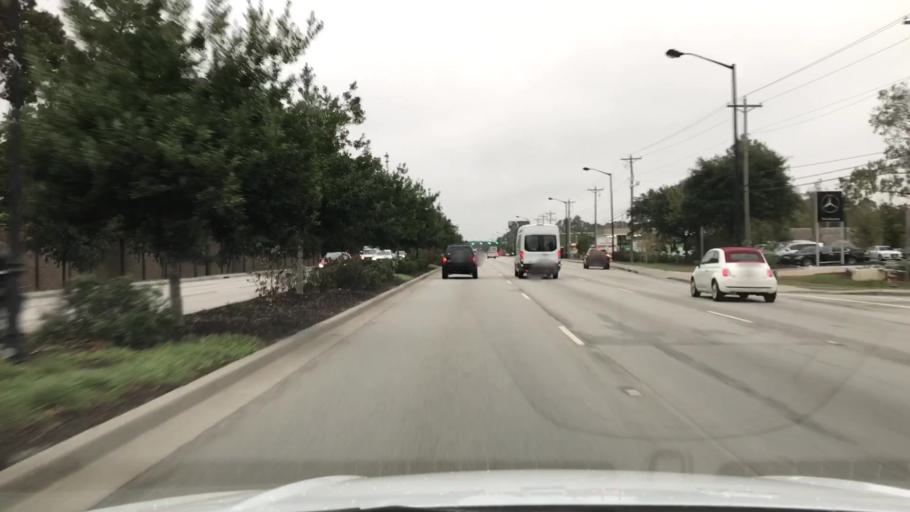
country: US
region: South Carolina
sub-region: Charleston County
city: Isle of Palms
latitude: 32.8393
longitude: -79.8196
